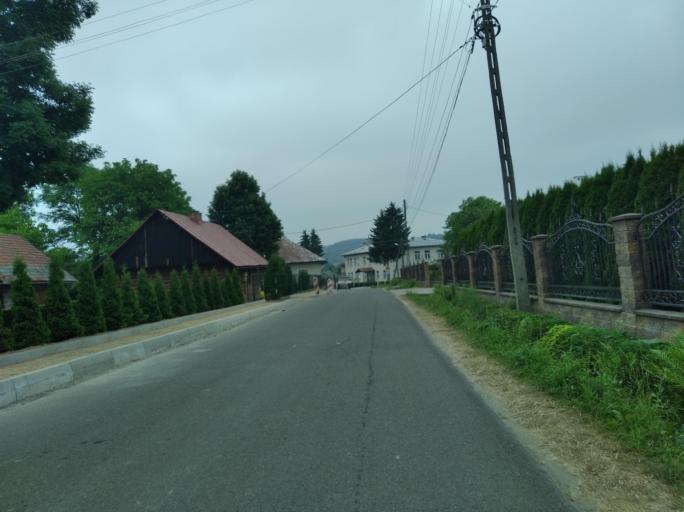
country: PL
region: Subcarpathian Voivodeship
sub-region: Powiat brzozowski
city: Jablonica Polska
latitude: 49.7010
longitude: 21.8975
